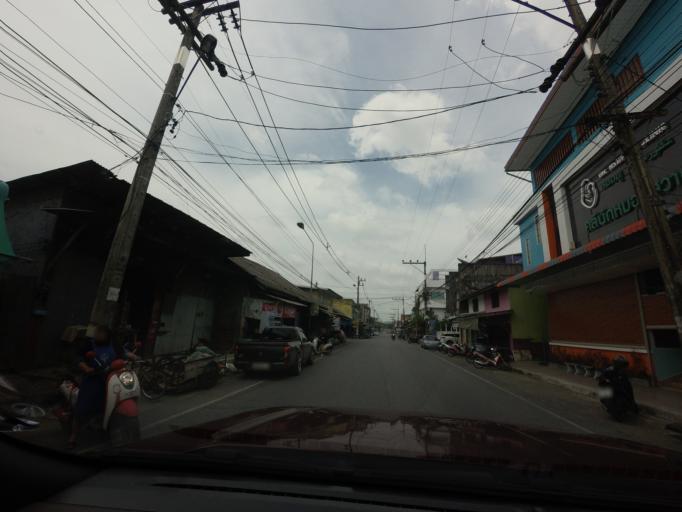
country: TH
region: Yala
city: Yala
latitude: 6.5639
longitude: 101.2938
